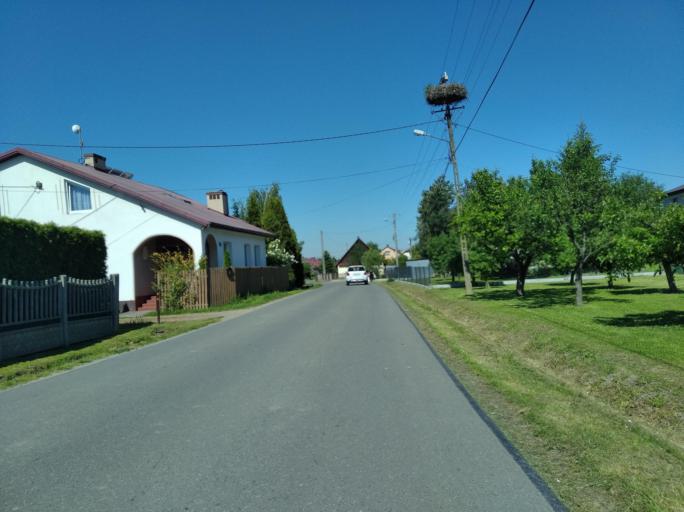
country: PL
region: Subcarpathian Voivodeship
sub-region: Krosno
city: Krosno
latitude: 49.7213
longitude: 21.7684
